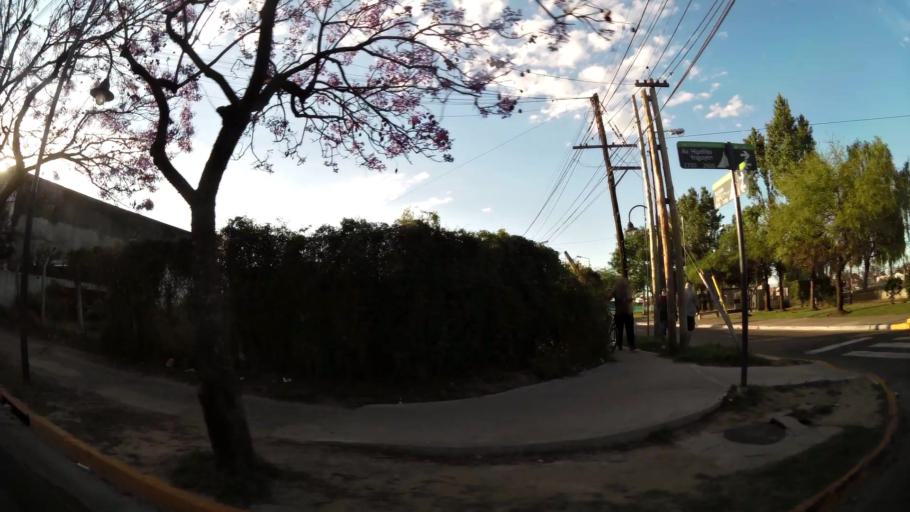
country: AR
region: Buenos Aires
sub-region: Partido de Tigre
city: Tigre
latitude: -34.4498
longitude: -58.5682
